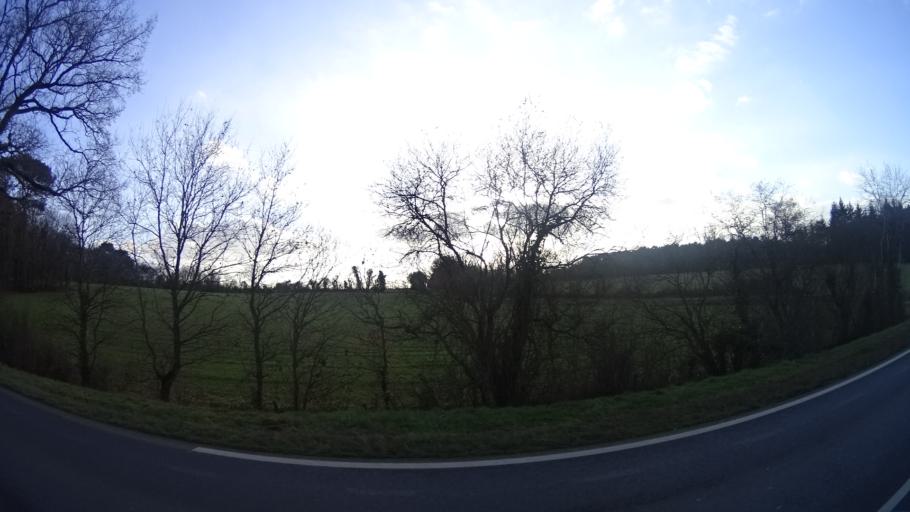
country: FR
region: Pays de la Loire
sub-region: Departement de la Loire-Atlantique
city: Fegreac
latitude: 47.6087
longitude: -2.0364
